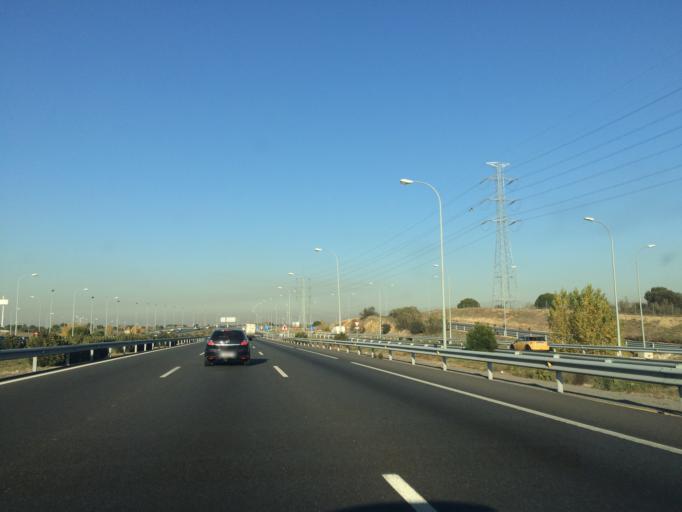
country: ES
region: Madrid
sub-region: Provincia de Madrid
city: Pozuelo de Alarcon
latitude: 40.4017
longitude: -3.8315
